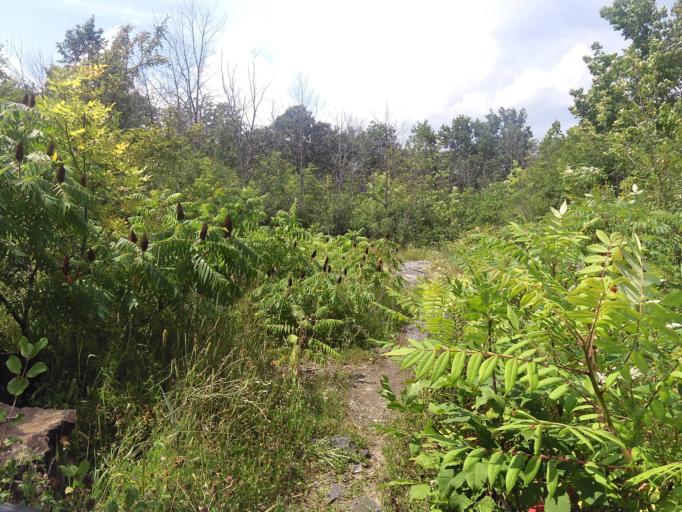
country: CA
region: Ontario
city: Bells Corners
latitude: 45.3180
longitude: -75.9205
